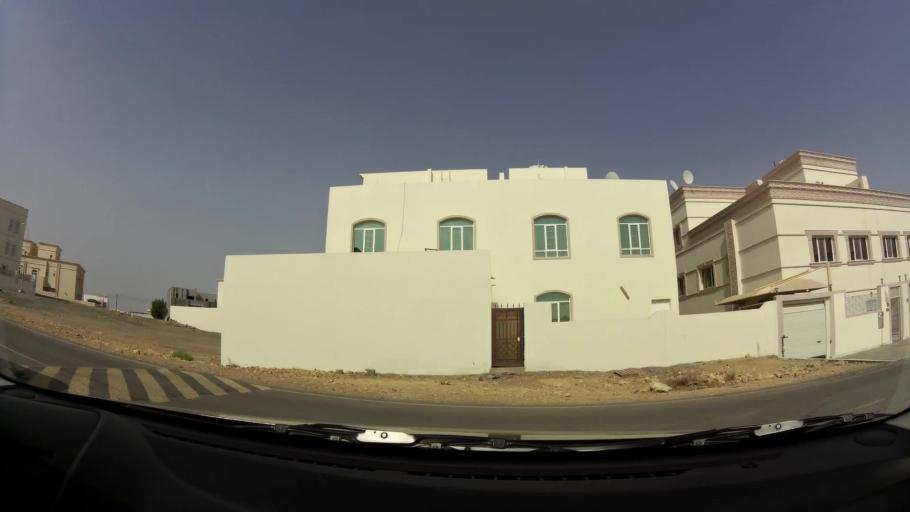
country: OM
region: Muhafazat Masqat
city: Bawshar
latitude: 23.5599
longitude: 58.3615
